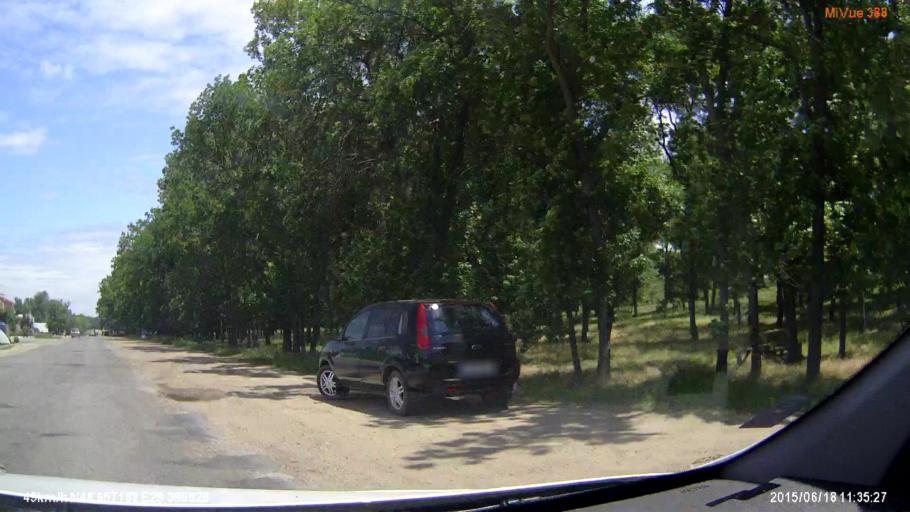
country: MD
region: Causeni
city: Causeni
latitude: 46.6570
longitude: 29.3965
